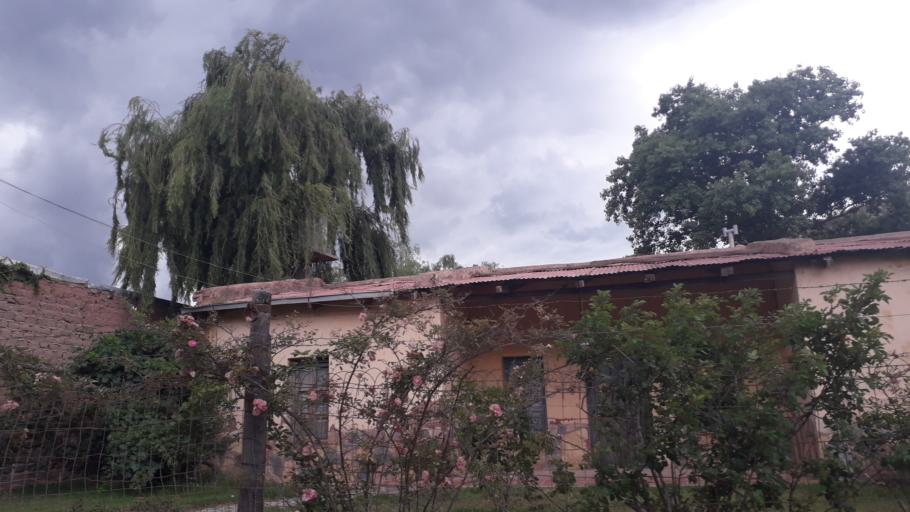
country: AR
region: Jujuy
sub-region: Departamento de Tumbaya
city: Tumbaya
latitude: -23.8580
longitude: -65.4676
